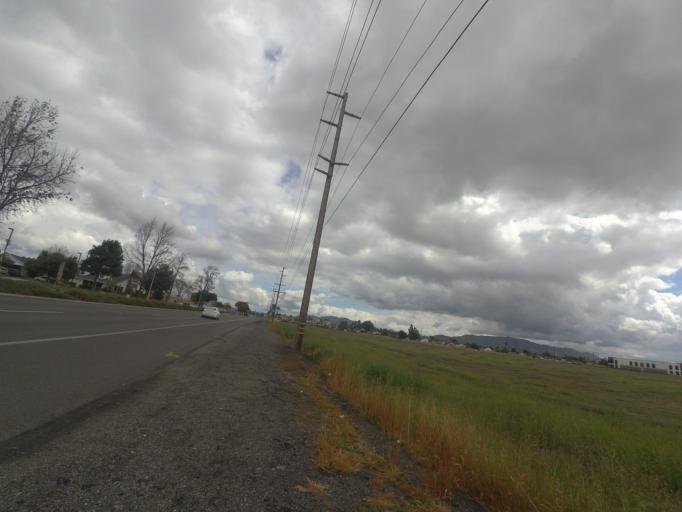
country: US
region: California
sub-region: Riverside County
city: Moreno Valley
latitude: 33.9171
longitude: -117.2473
